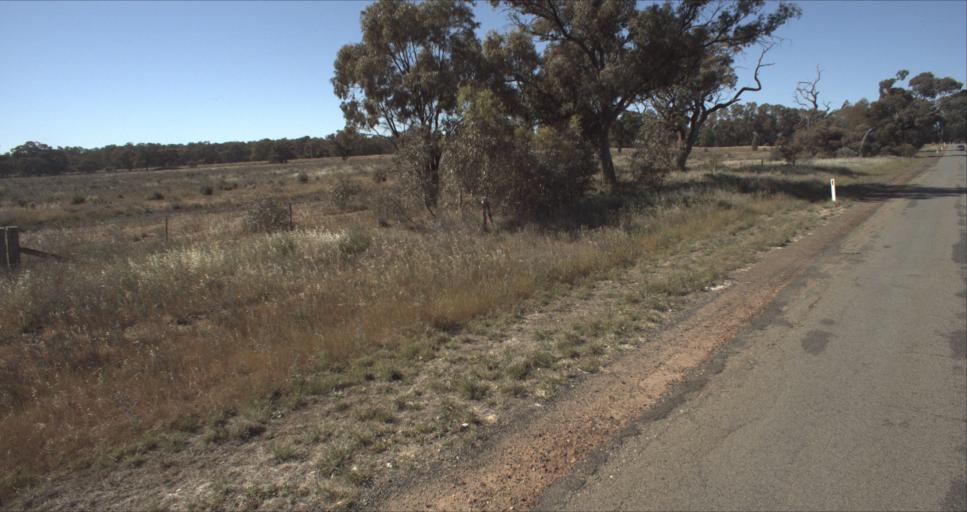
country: AU
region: New South Wales
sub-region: Leeton
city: Leeton
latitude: -34.6023
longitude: 146.2574
